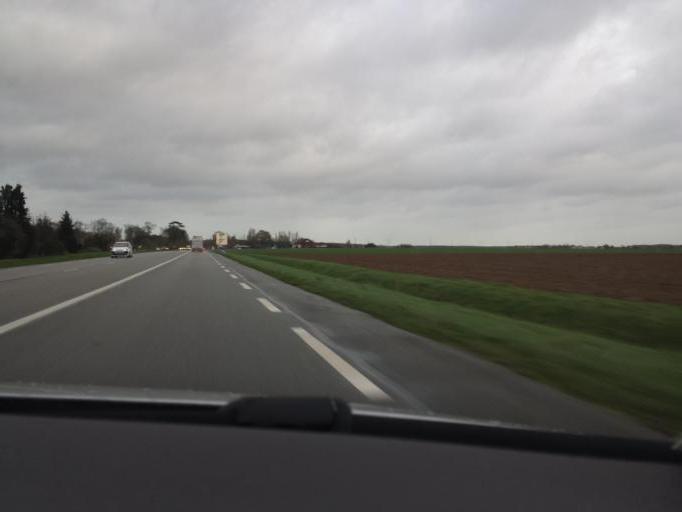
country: FR
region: Haute-Normandie
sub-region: Departement de l'Eure
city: Gravigny
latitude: 49.0142
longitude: 1.2329
